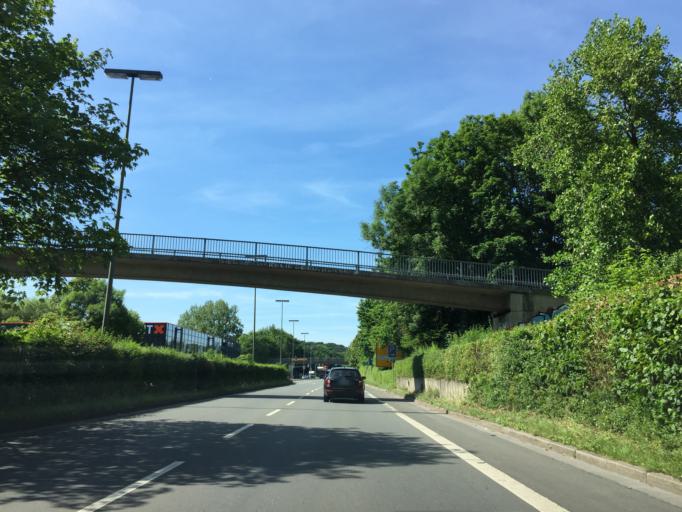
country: DE
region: North Rhine-Westphalia
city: Iserlohn
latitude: 51.3846
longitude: 7.7131
